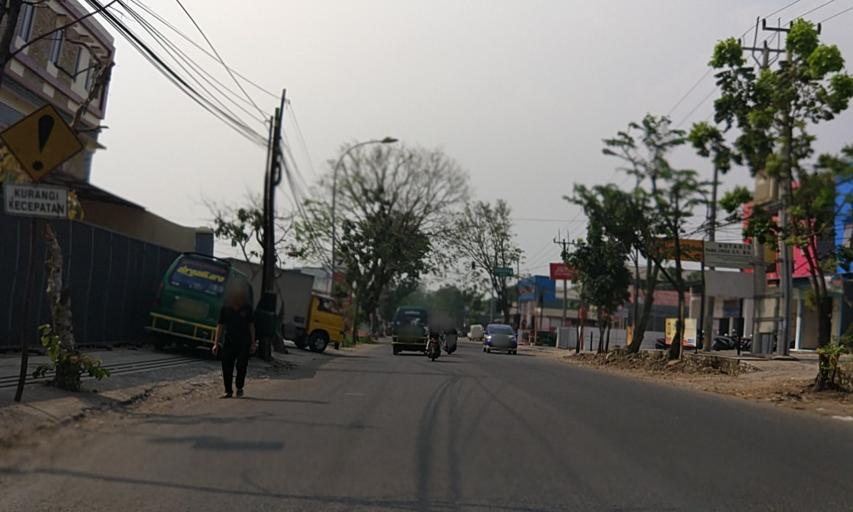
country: ID
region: West Java
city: Margahayukencana
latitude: -7.0050
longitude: 107.5520
